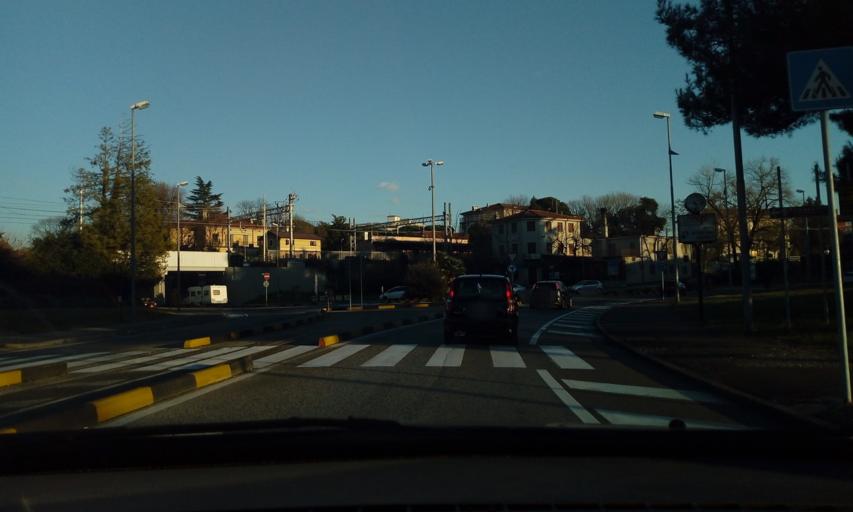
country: IT
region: Friuli Venezia Giulia
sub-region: Provincia di Gorizia
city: Gorizia
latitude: 45.9336
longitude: 13.6047
